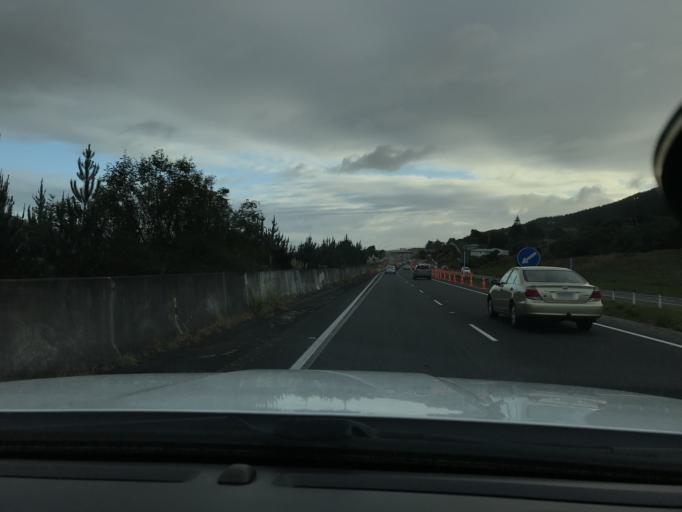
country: NZ
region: Wellington
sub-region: Porirua City
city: Porirua
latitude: -41.1660
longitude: 174.8332
